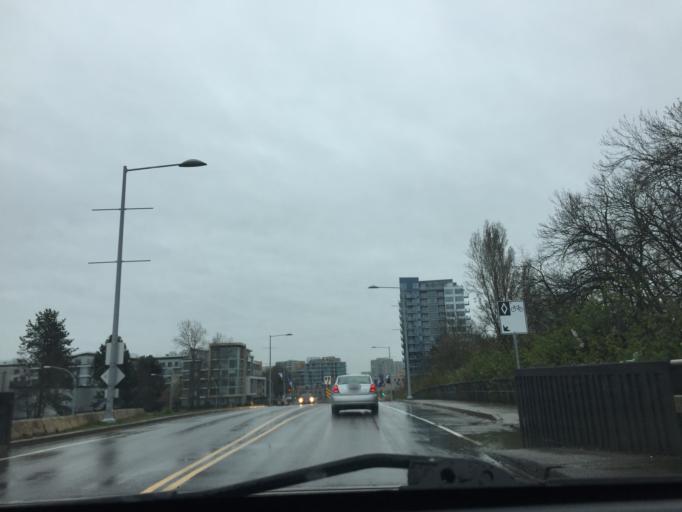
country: CA
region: British Columbia
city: Richmond
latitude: 49.1775
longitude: -123.1475
